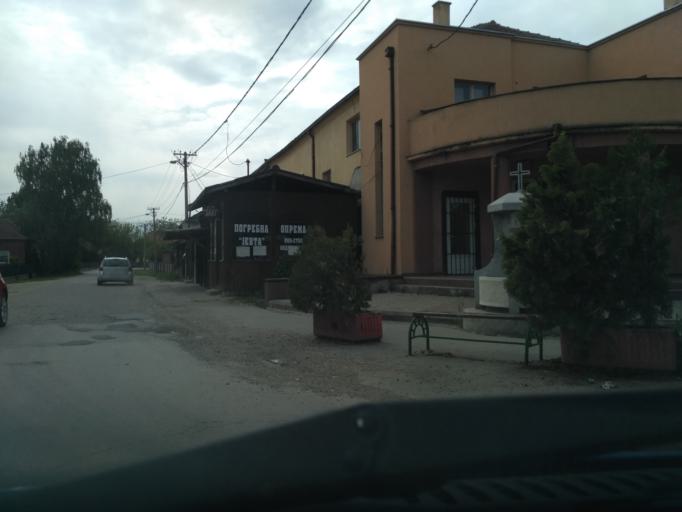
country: RS
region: Central Serbia
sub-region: Podunavski Okrug
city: Velika Plana
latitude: 44.3711
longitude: 21.0896
